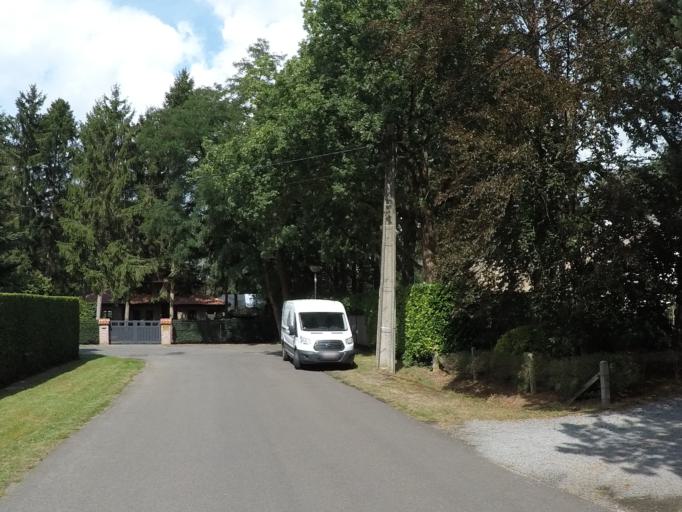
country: BE
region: Flanders
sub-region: Provincie Antwerpen
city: Zandhoven
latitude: 51.1971
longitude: 4.6870
